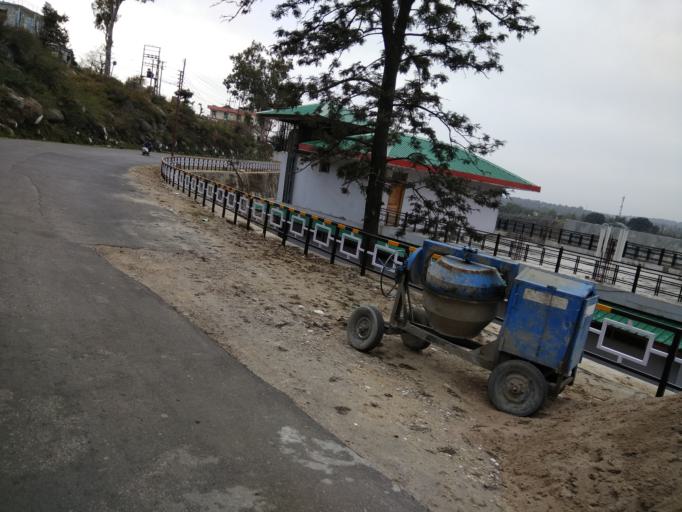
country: IN
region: Himachal Pradesh
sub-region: Kangra
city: Dharmsala
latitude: 32.1475
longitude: 76.4227
